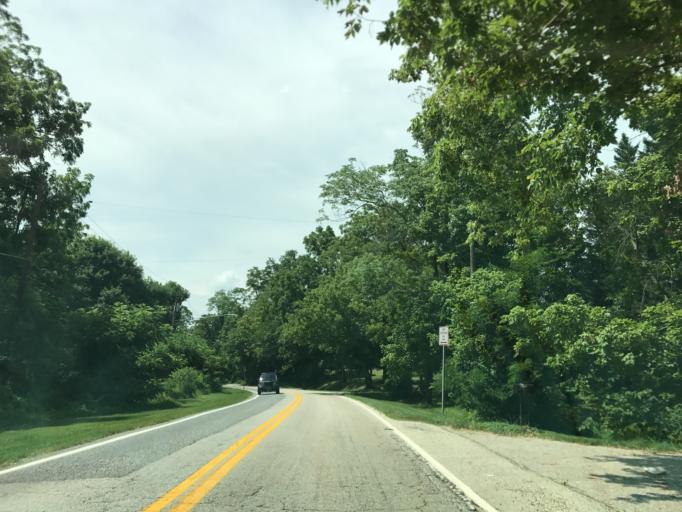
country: US
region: Maryland
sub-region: Baltimore County
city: Cockeysville
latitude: 39.4951
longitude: -76.6817
